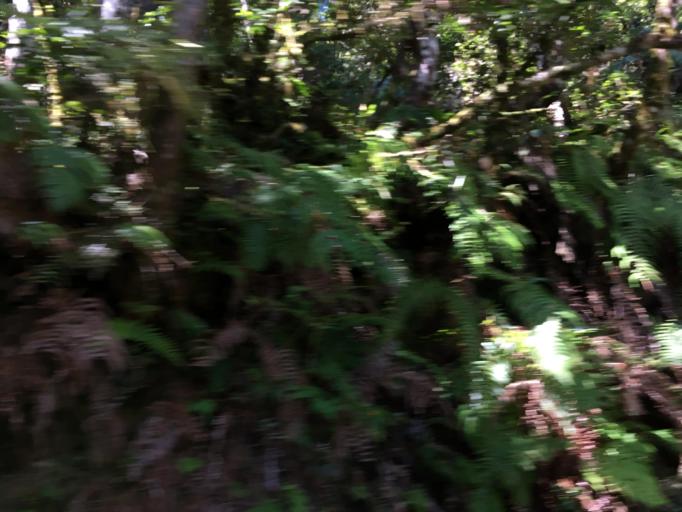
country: TW
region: Taiwan
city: Daxi
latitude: 24.5494
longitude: 121.3989
